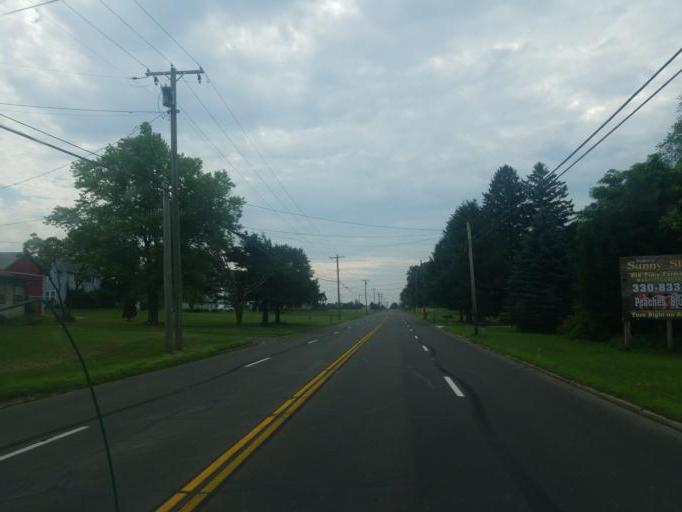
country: US
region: Ohio
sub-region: Wayne County
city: Dalton
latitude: 40.7987
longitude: -81.6428
